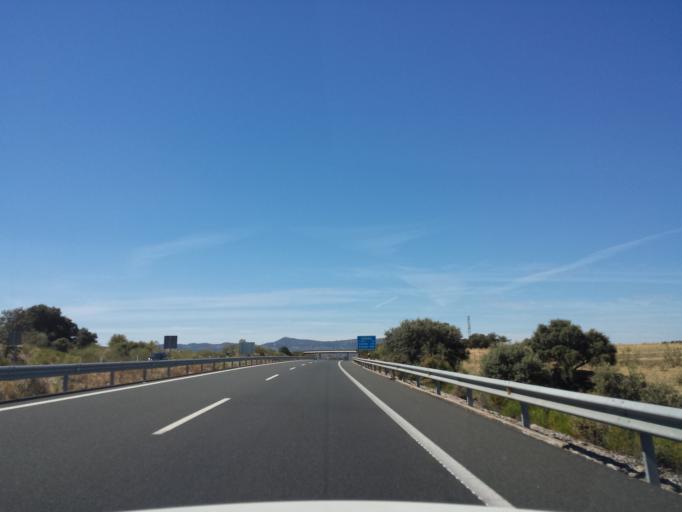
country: ES
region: Extremadura
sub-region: Provincia de Caceres
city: Almaraz
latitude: 39.8012
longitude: -5.6749
